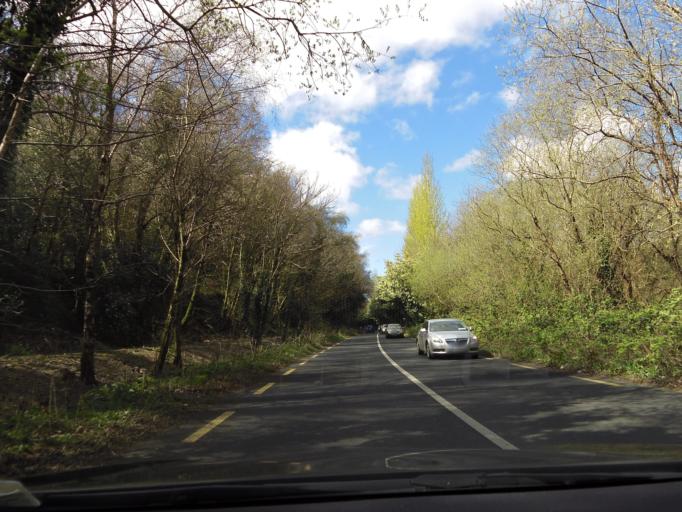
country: IE
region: Leinster
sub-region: Wicklow
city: Arklow
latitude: 52.8110
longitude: -6.1904
